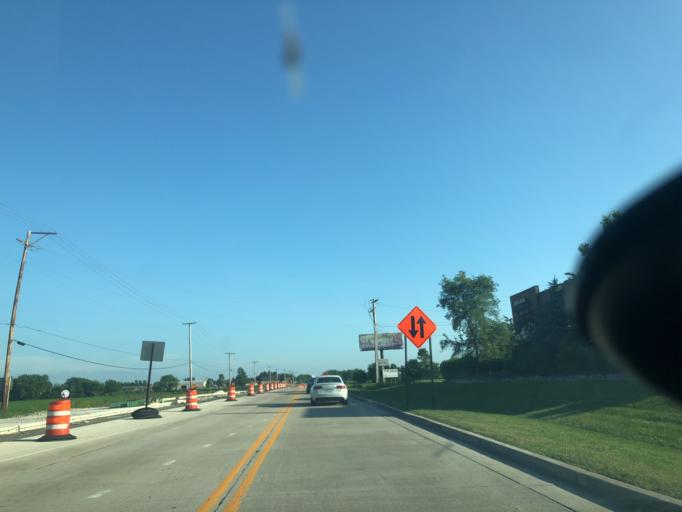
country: US
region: Illinois
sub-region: Will County
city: Homer Glen
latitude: 41.5996
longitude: -87.8915
